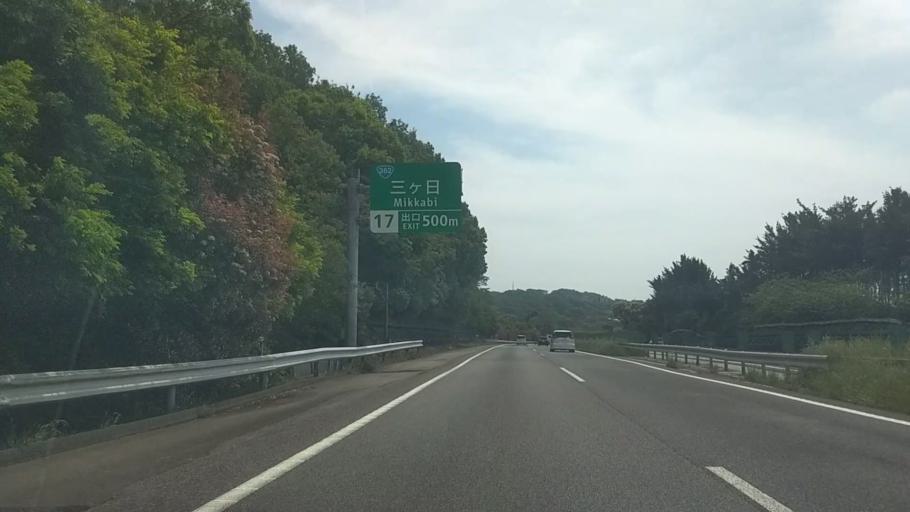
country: JP
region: Shizuoka
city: Kosai-shi
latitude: 34.8024
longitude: 137.5732
